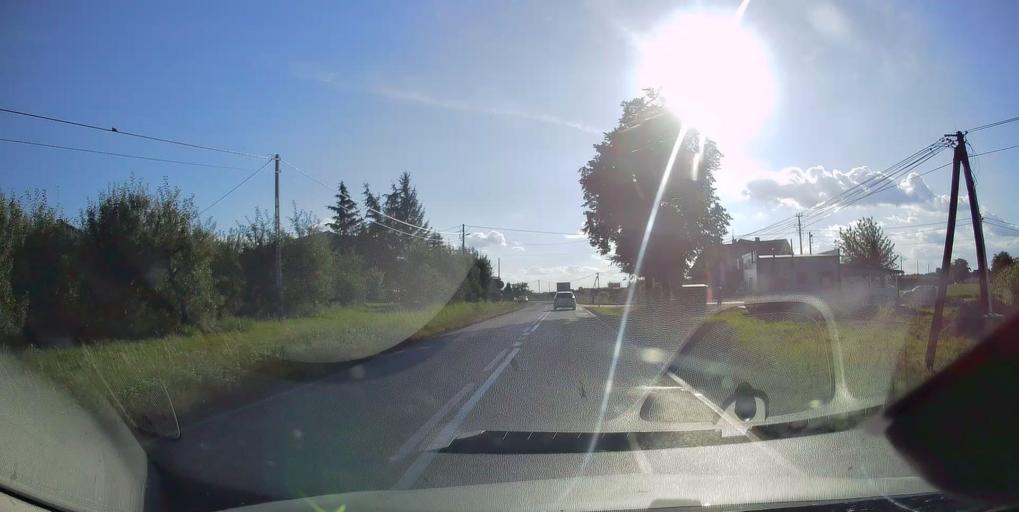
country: PL
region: Masovian Voivodeship
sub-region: Powiat grojecki
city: Bledow
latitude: 51.8142
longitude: 20.7332
